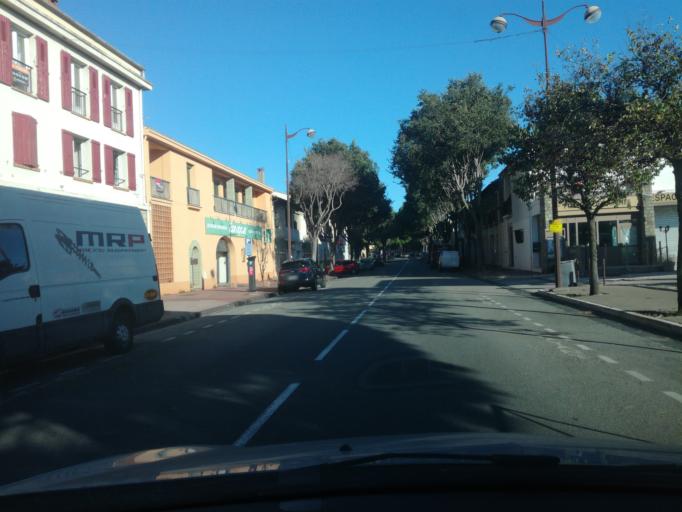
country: FR
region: Provence-Alpes-Cote d'Azur
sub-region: Departement du Var
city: Frejus
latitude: 43.4335
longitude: 6.7283
